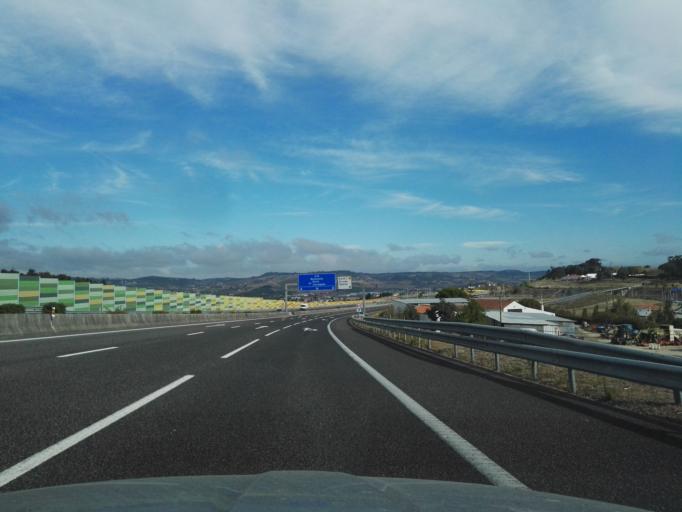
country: PT
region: Lisbon
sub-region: Arruda Dos Vinhos
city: Arruda dos Vinhos
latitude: 38.9616
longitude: -9.0627
